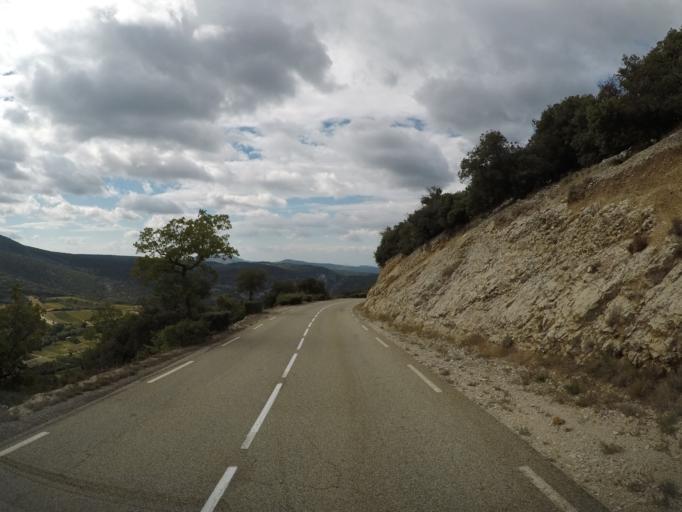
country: FR
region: Rhone-Alpes
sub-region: Departement de la Drome
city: Buis-les-Baronnies
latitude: 44.2213
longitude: 5.2168
